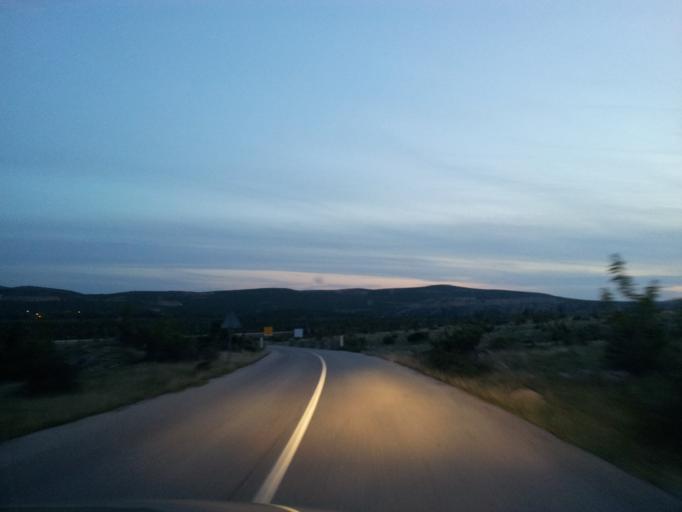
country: HR
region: Zadarska
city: Obrovac
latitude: 44.2202
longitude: 15.6685
